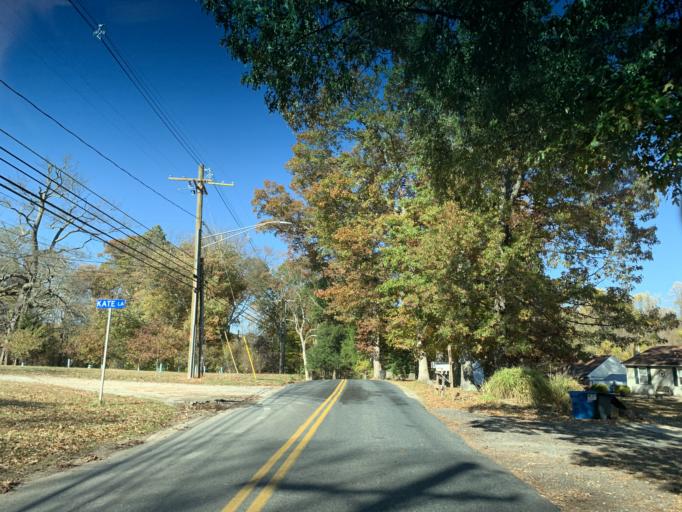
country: US
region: Maryland
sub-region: Harford County
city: Joppatowne
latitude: 39.4549
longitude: -76.3388
